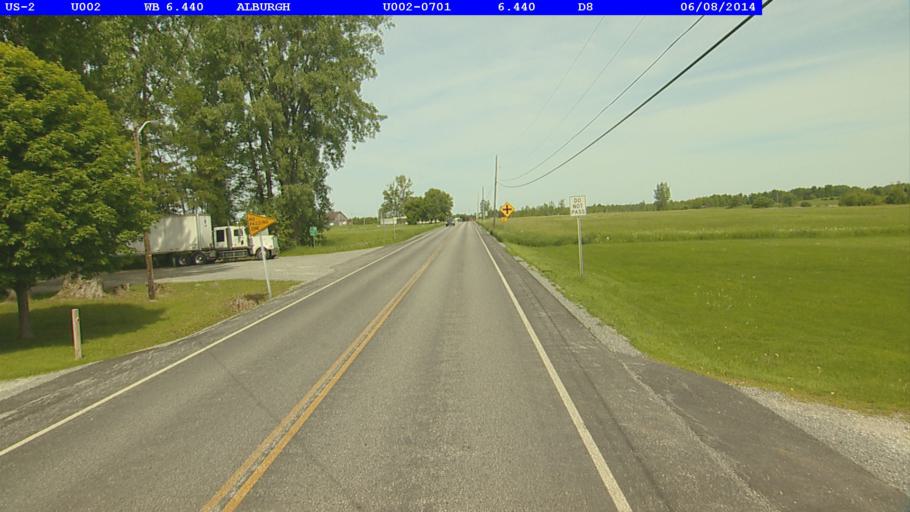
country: US
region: New York
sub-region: Clinton County
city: Rouses Point
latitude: 44.9575
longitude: -73.2744
